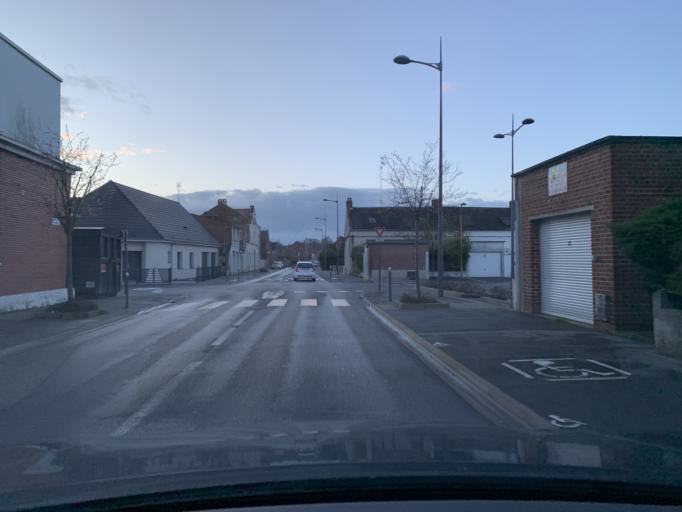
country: FR
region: Nord-Pas-de-Calais
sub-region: Departement du Nord
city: Cambrai
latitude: 50.1649
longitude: 3.2495
